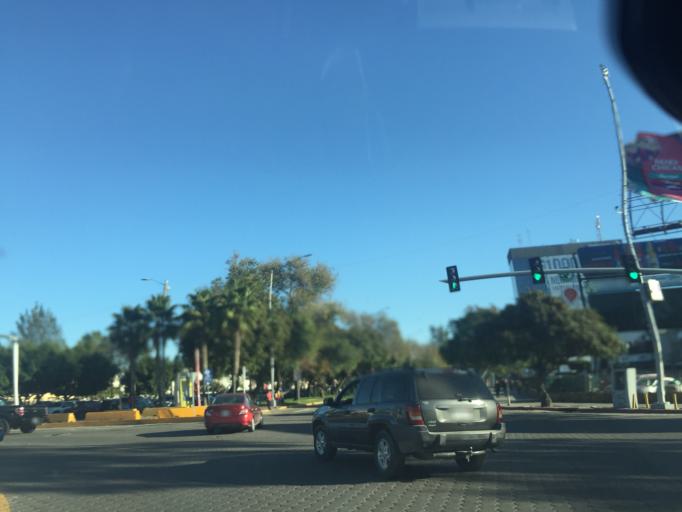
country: MX
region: Baja California
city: Tijuana
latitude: 32.5285
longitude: -117.0232
